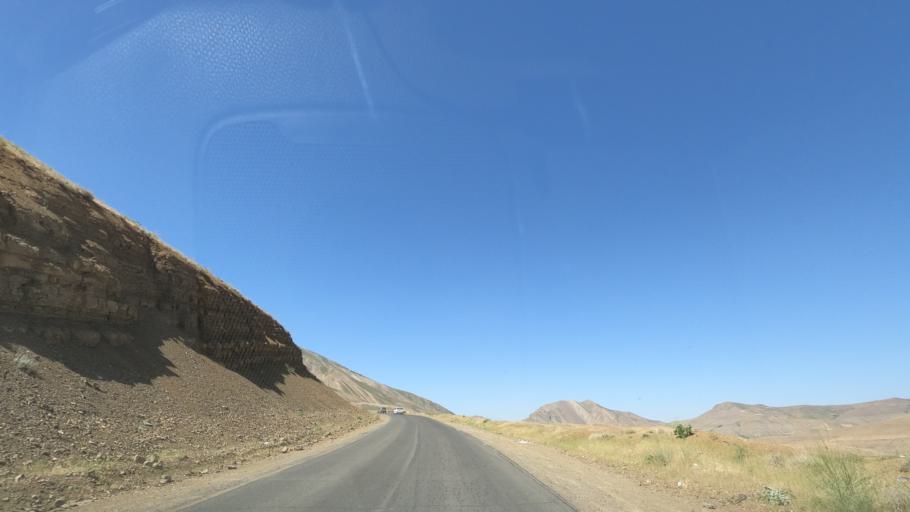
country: IR
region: Alborz
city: Karaj
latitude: 35.9312
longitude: 51.0864
